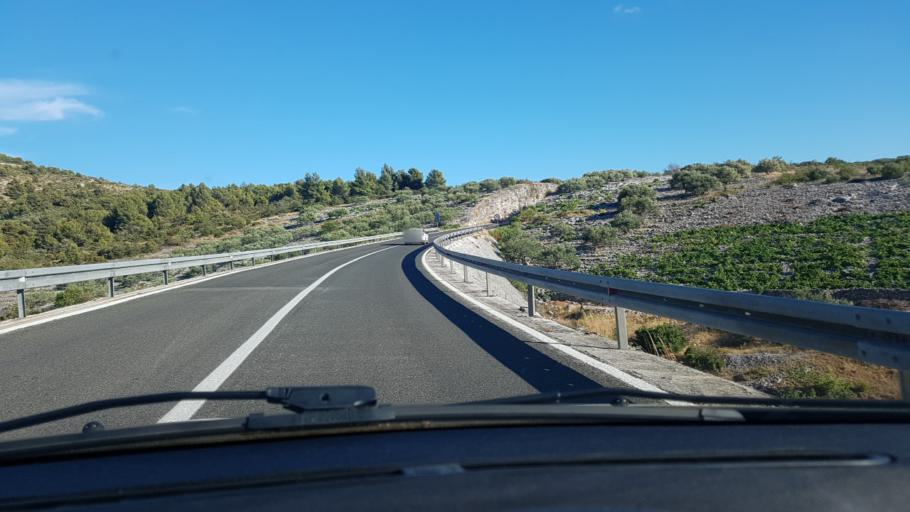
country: HR
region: Sibensko-Kniniska
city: Primosten
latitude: 43.5689
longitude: 15.9465
